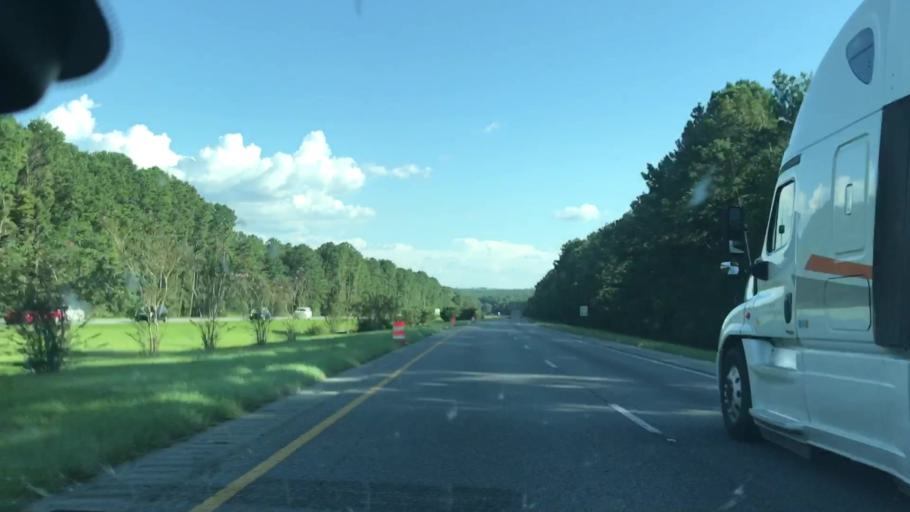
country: US
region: Georgia
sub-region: Harris County
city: Hamilton
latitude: 32.6503
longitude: -84.9727
